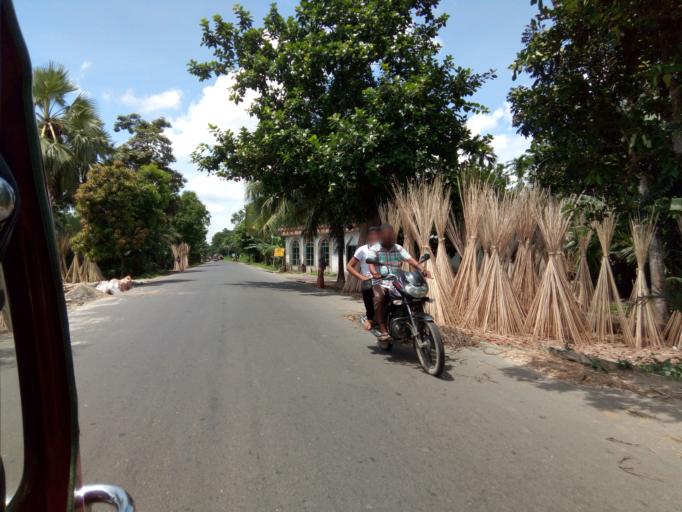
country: BD
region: Dhaka
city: Tungipara
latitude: 22.9023
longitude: 89.8851
